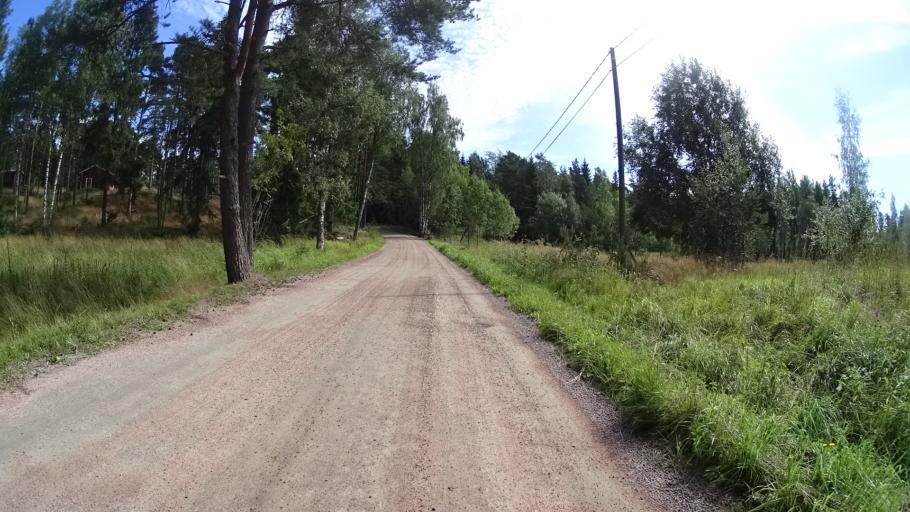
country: FI
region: Uusimaa
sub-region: Helsinki
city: Kirkkonummi
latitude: 60.0985
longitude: 24.5227
